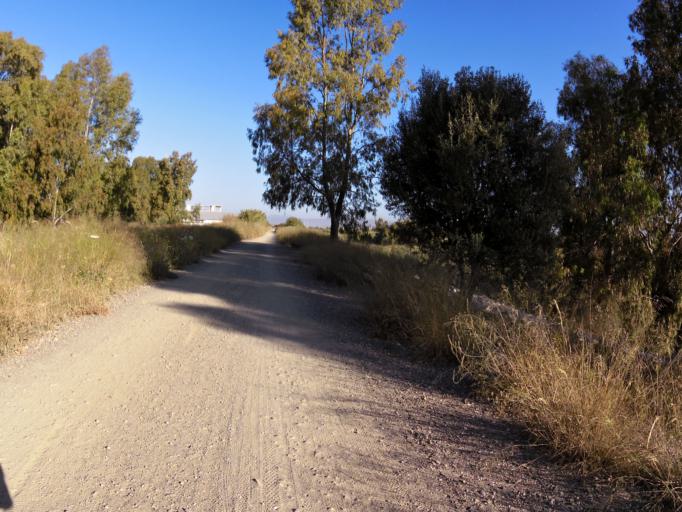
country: ES
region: Andalusia
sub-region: Provincia de Malaga
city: Torremolinos
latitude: 36.6752
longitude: -4.4705
